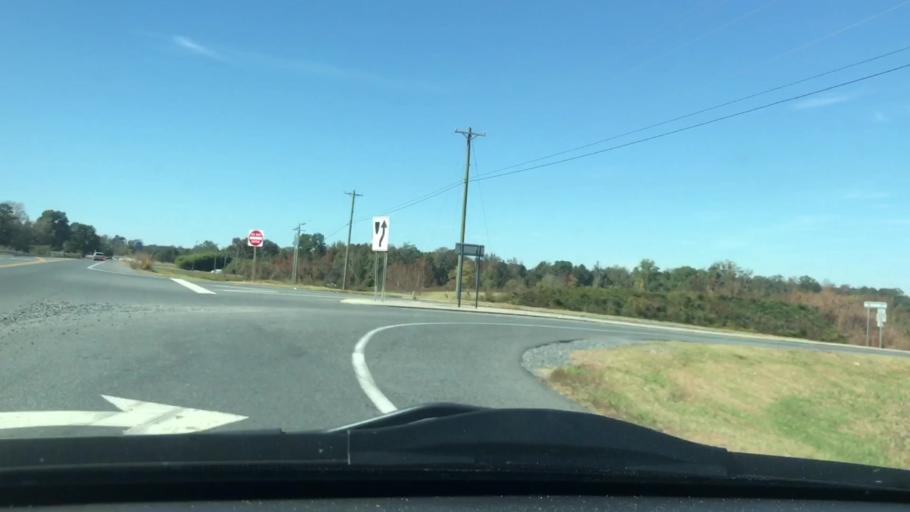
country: US
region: North Carolina
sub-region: Randolph County
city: Randleman
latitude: 35.8208
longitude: -79.8530
